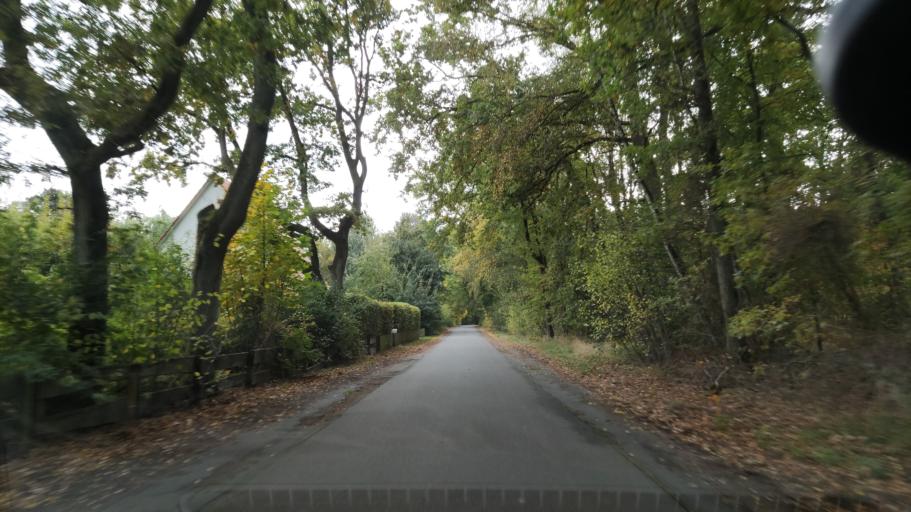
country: DE
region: Lower Saxony
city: Jelmstorf
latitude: 53.1360
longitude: 10.5297
